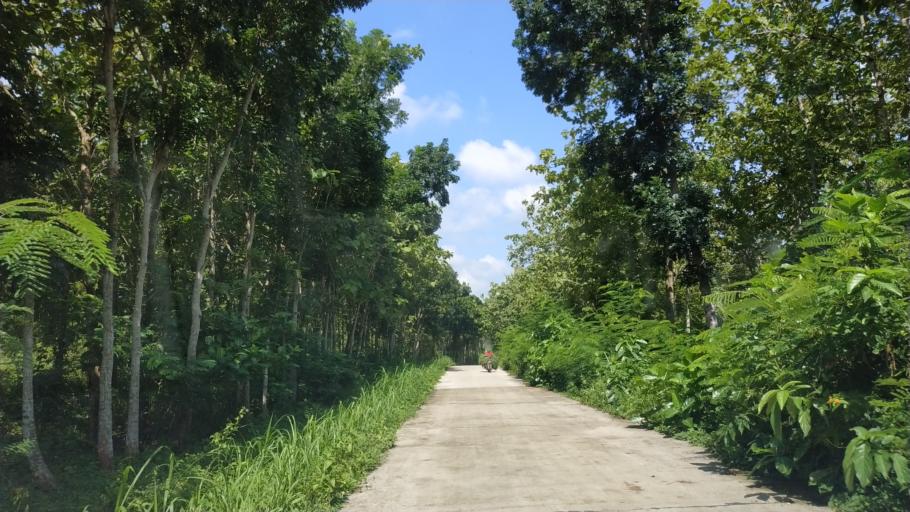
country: ID
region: Central Java
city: Guyangan
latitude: -7.0006
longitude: 111.0860
